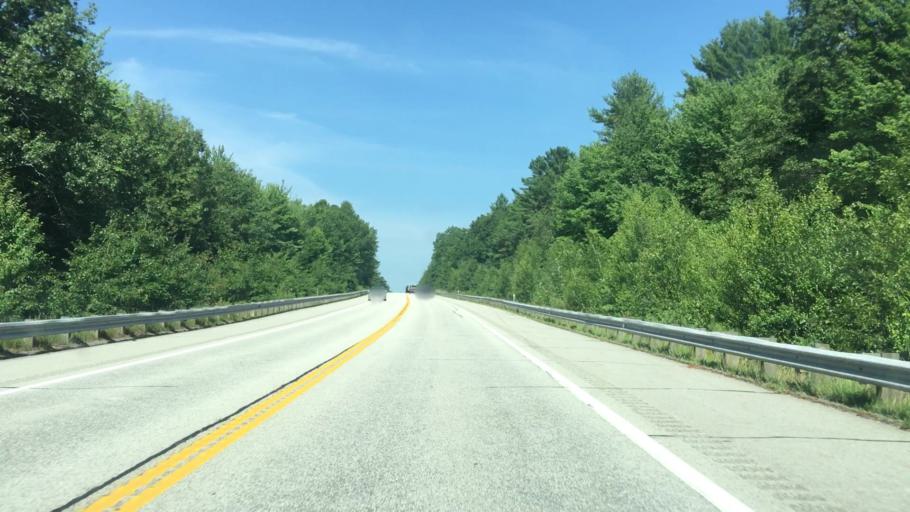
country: US
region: New Hampshire
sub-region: Merrimack County
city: Henniker
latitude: 43.1813
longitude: -71.7667
